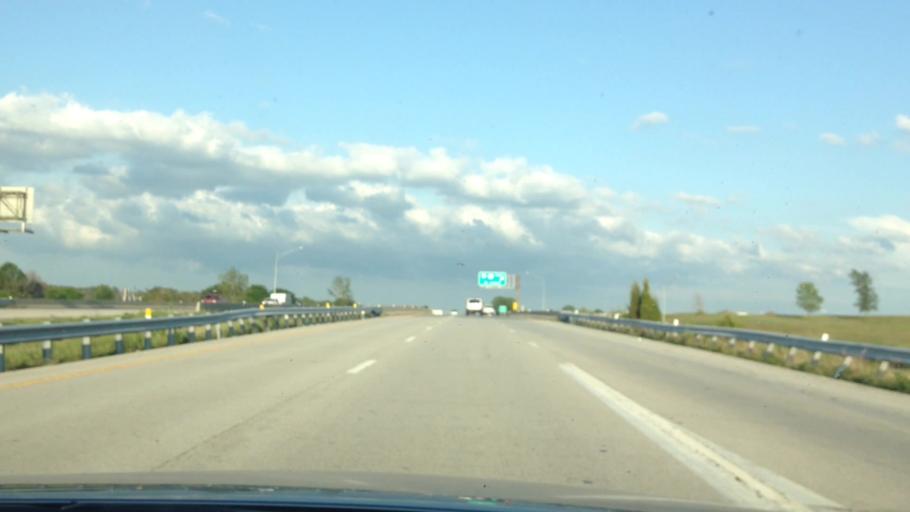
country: US
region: Missouri
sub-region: Platte County
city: Weatherby Lake
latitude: 39.2544
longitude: -94.6597
